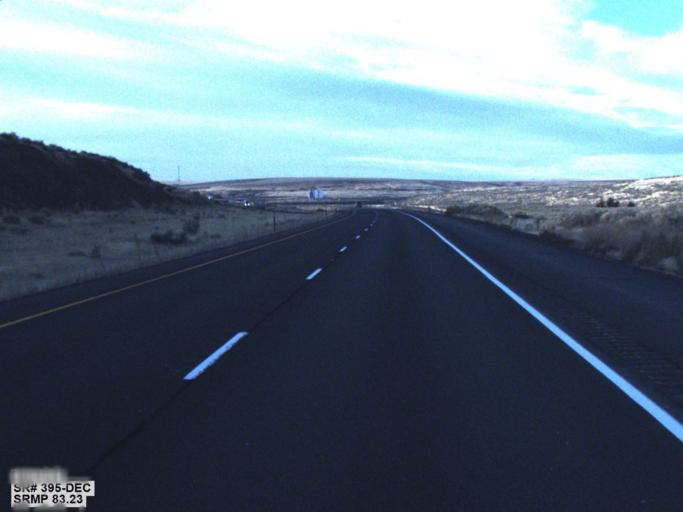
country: US
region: Washington
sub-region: Adams County
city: Ritzville
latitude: 46.9845
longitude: -118.5602
